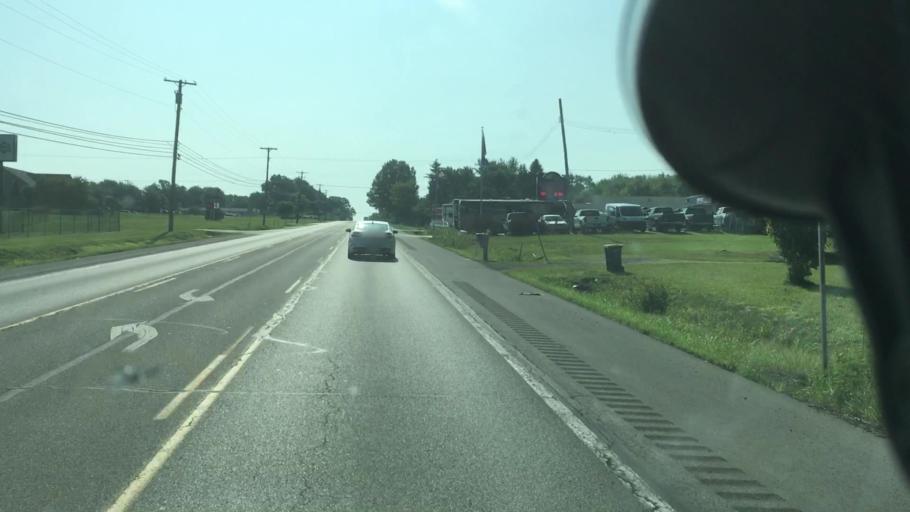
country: US
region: Pennsylvania
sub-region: Lawrence County
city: New Castle
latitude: 40.9761
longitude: -80.2848
